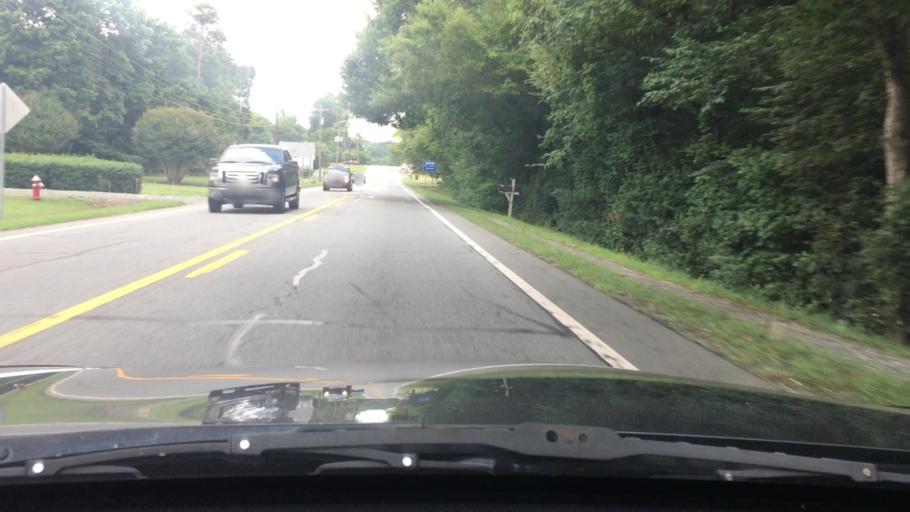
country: US
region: North Carolina
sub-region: Alamance County
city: Haw River
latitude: 36.0932
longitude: -79.3439
